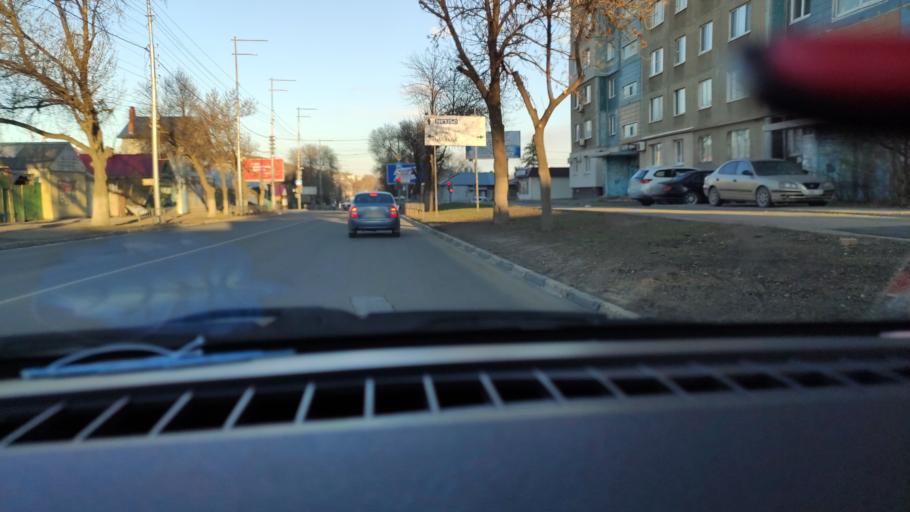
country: RU
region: Saratov
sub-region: Saratovskiy Rayon
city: Saratov
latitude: 51.5449
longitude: 46.0298
